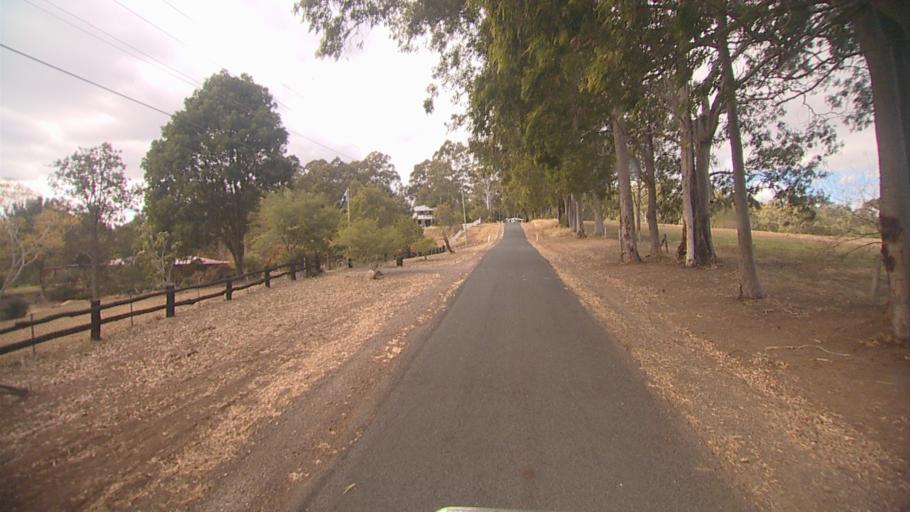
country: AU
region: Queensland
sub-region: Logan
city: Cedar Vale
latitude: -27.9021
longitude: 153.0269
